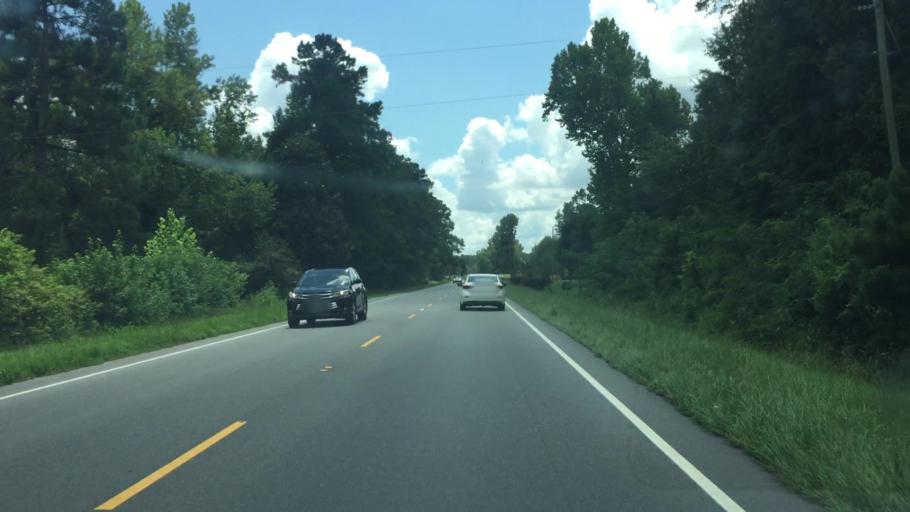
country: US
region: North Carolina
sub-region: Columbus County
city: Tabor City
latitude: 34.1910
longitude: -78.8364
